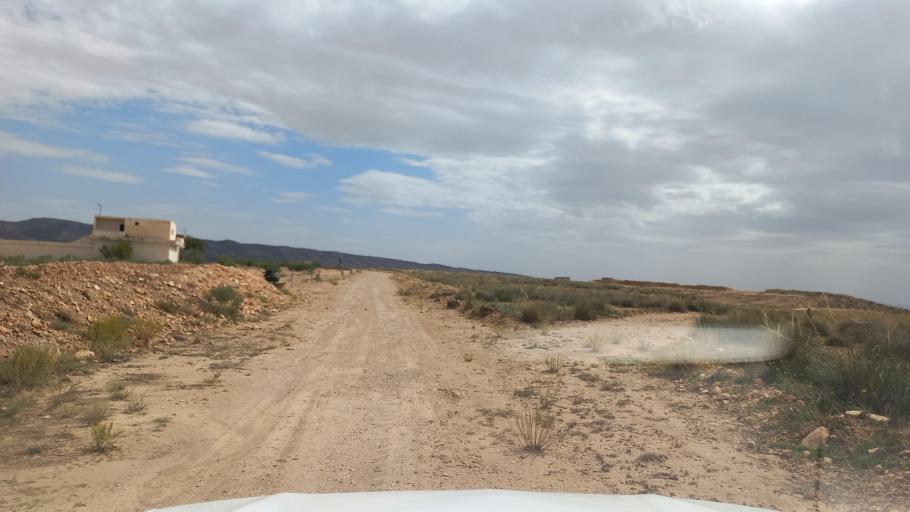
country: TN
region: Al Qasrayn
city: Sbiba
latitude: 35.3603
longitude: 9.1129
